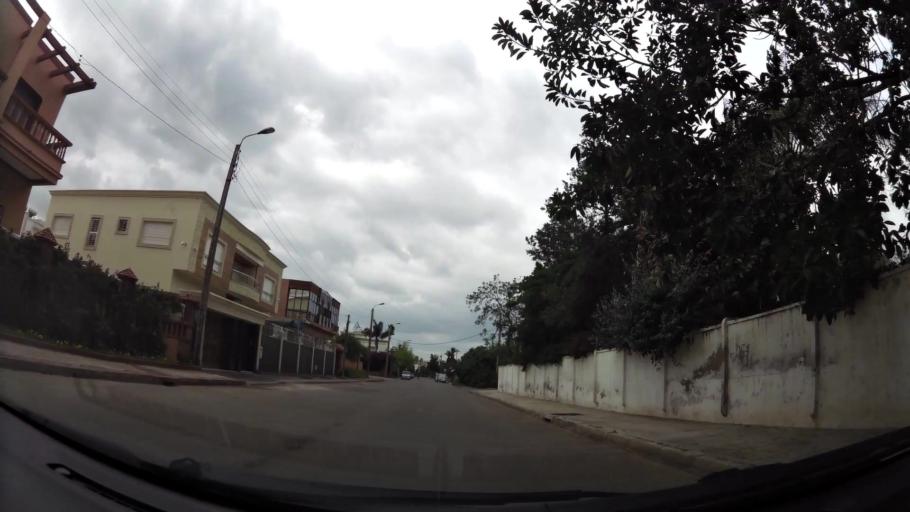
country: MA
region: Grand Casablanca
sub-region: Casablanca
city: Casablanca
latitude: 33.5564
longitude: -7.6161
